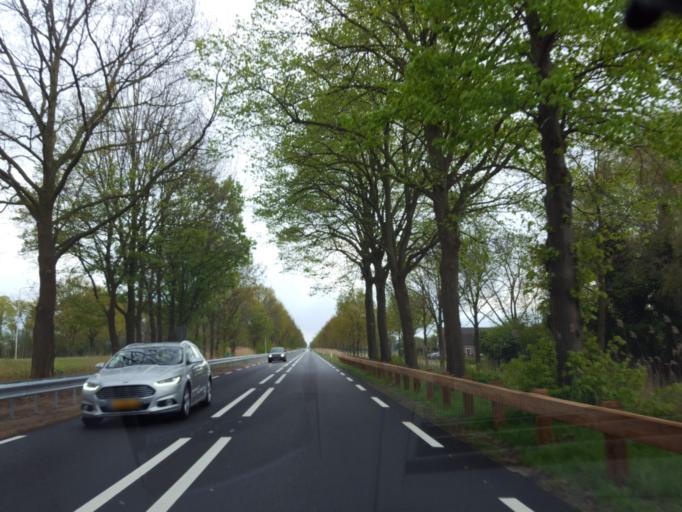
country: NL
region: North Brabant
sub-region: Gemeente Someren
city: Someren
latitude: 51.3491
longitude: 5.7432
